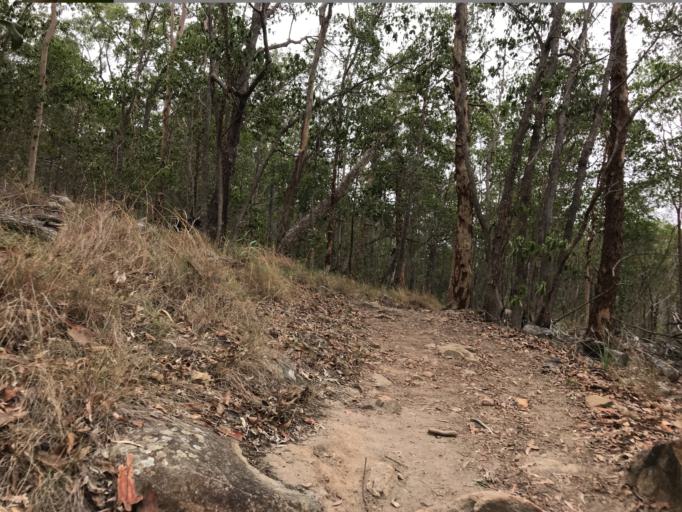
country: AU
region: Queensland
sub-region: Brisbane
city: Taringa
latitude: -27.4644
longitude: 152.9534
